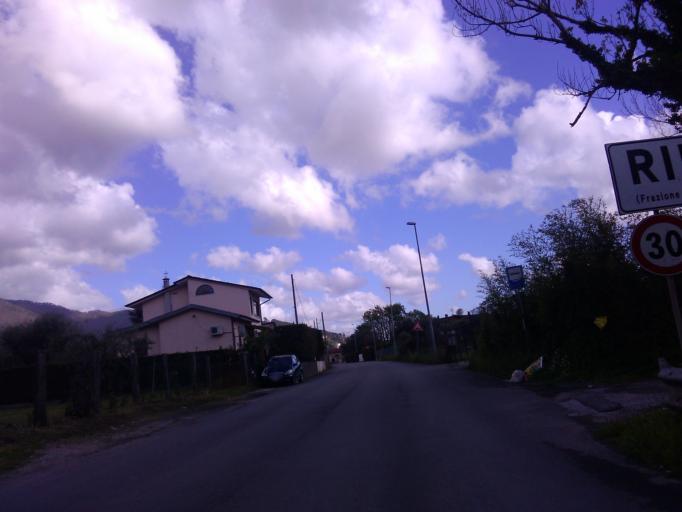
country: IT
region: Tuscany
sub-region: Provincia di Lucca
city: Ripa-Pozzi-Querceta-Ponterosso
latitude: 43.9866
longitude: 10.2073
